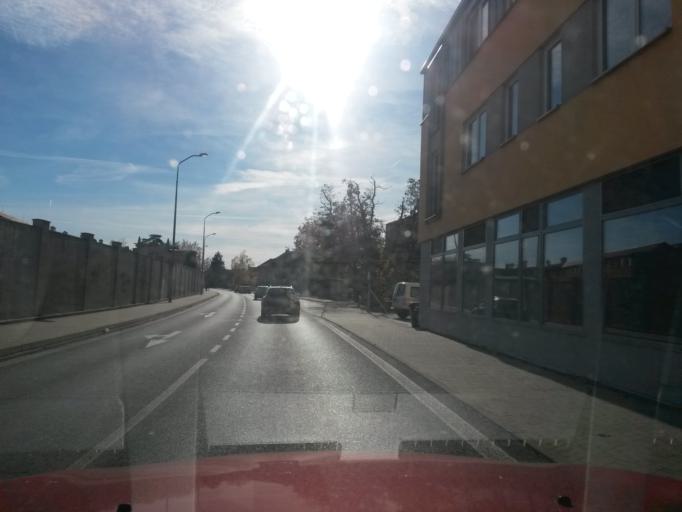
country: SK
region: Presovsky
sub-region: Okres Presov
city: Presov
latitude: 48.9979
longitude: 21.2357
